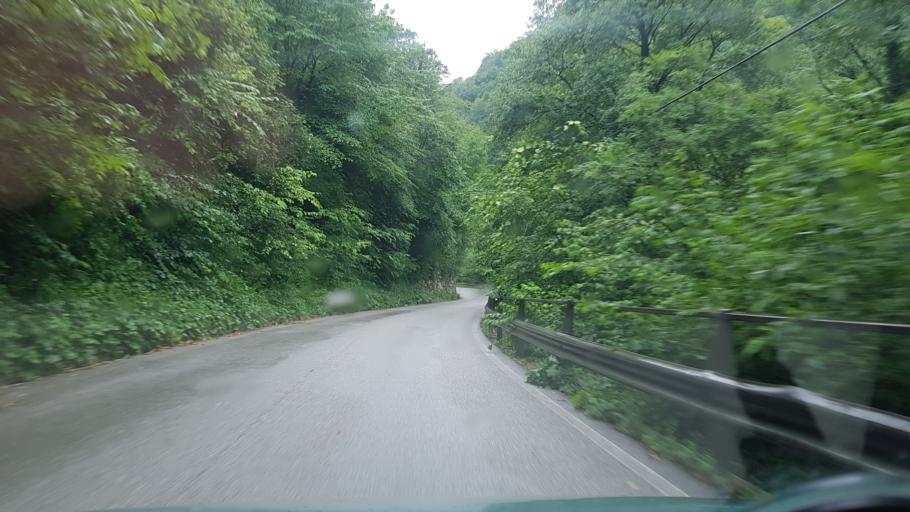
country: IT
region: Friuli Venezia Giulia
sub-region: Provincia di Udine
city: Lusevera
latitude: 46.2408
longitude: 13.2943
